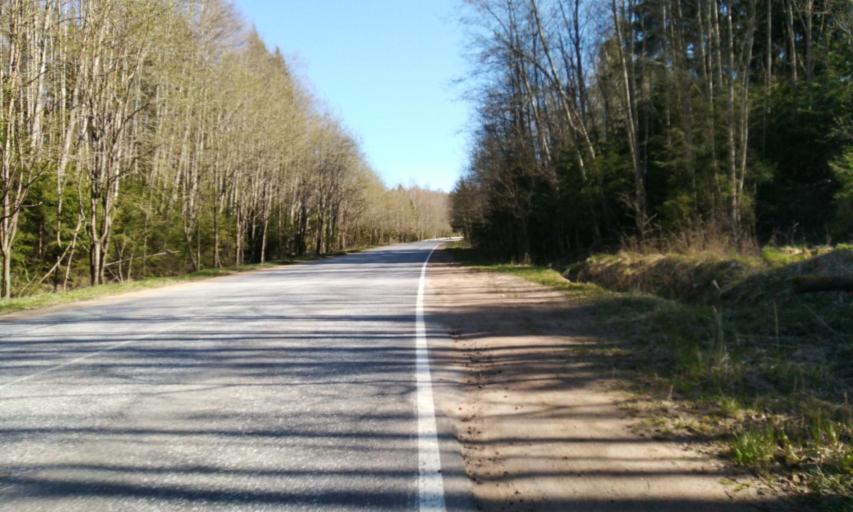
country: RU
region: Leningrad
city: Garbolovo
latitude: 60.3697
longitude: 30.4411
